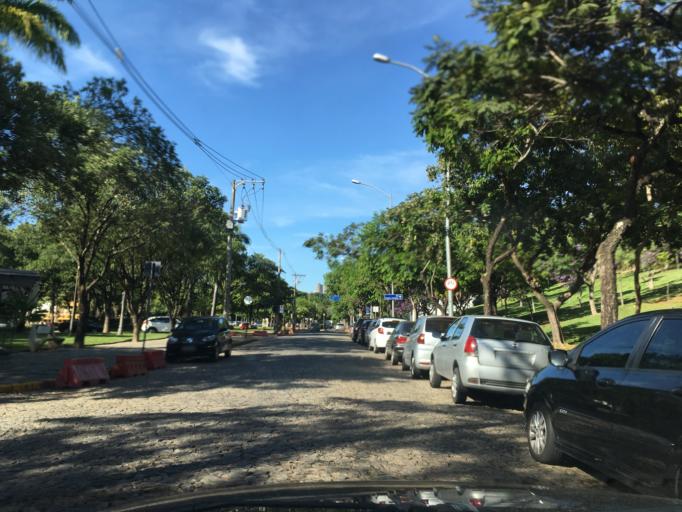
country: BR
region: Minas Gerais
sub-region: Belo Horizonte
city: Belo Horizonte
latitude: -19.8654
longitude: -43.9648
